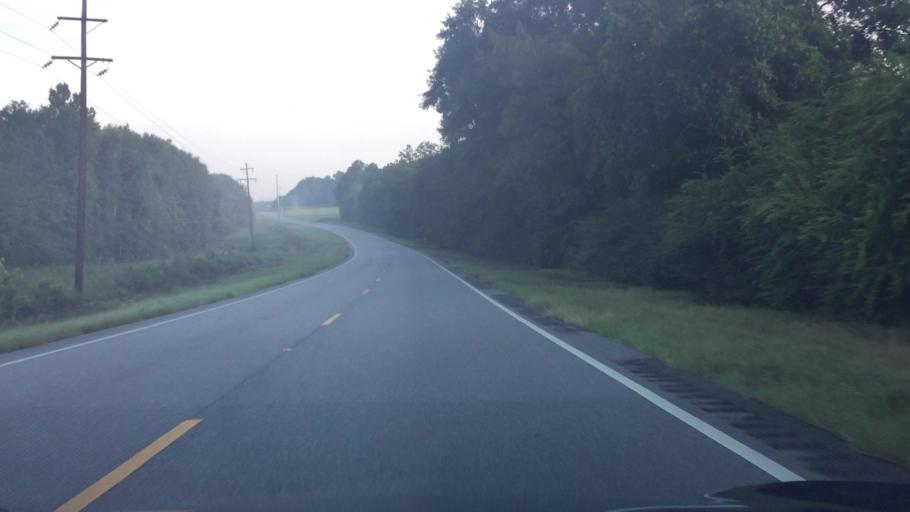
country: US
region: Alabama
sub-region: Covington County
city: Florala
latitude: 31.0716
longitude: -86.4049
